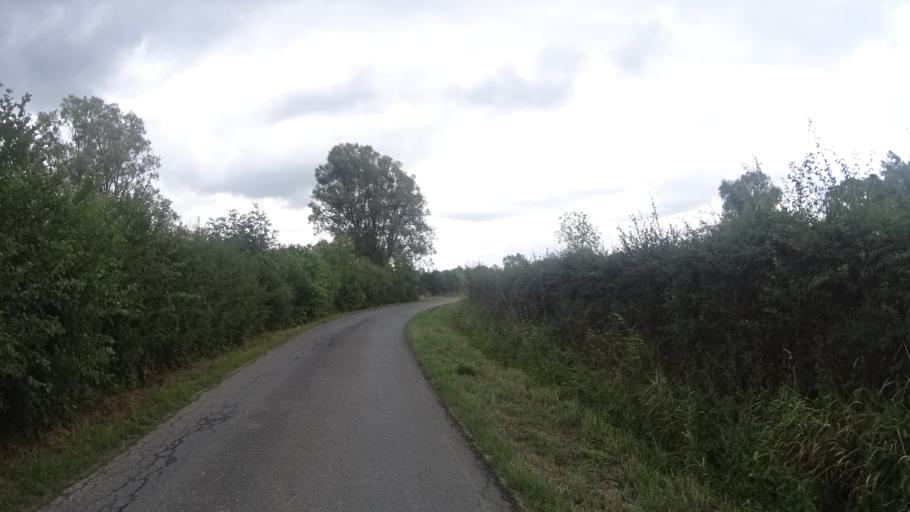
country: FR
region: Nord-Pas-de-Calais
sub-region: Departement du Nord
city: Maroilles
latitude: 50.1436
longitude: 3.7438
